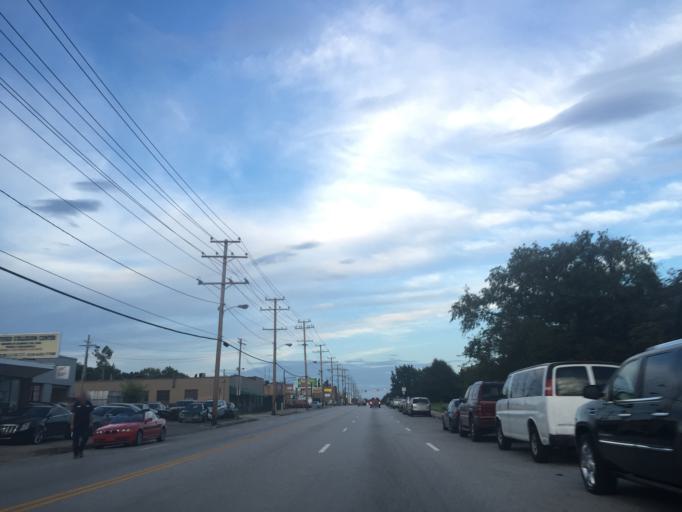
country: US
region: Maryland
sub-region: Baltimore County
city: Dundalk
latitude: 39.2722
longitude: -76.5392
